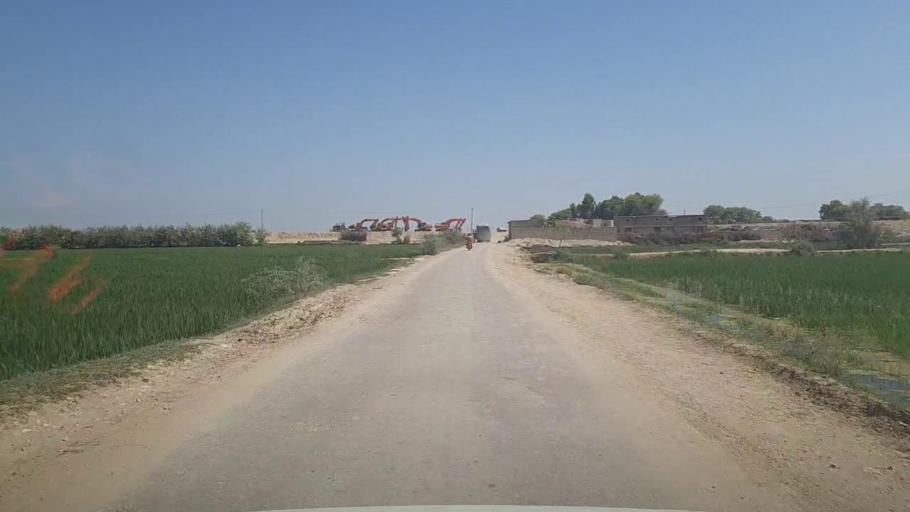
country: PK
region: Sindh
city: Kashmor
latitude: 28.2807
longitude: 69.4428
